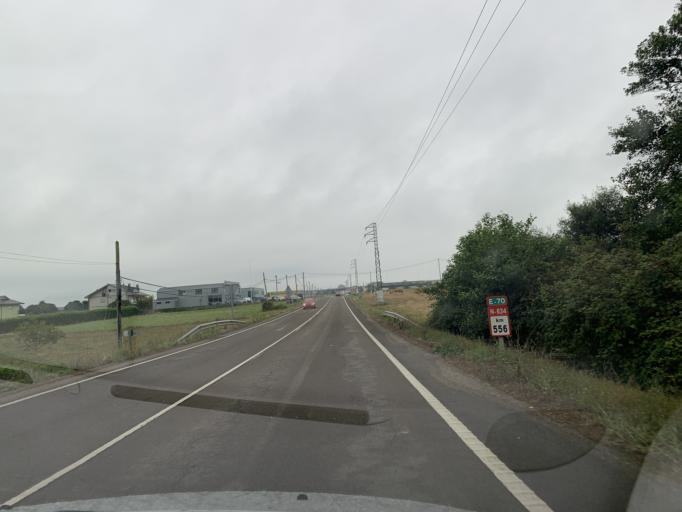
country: ES
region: Galicia
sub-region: Provincia de Lugo
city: Ribadeo
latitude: 43.5427
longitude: -7.0748
